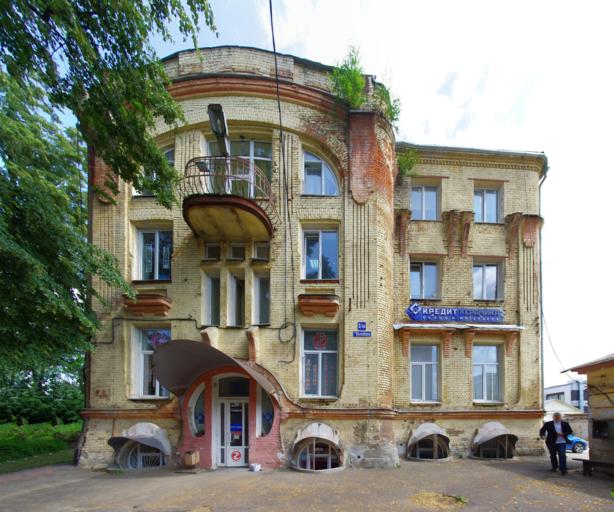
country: RU
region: Nizjnij Novgorod
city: Nizhniy Novgorod
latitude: 56.3074
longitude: 43.9879
